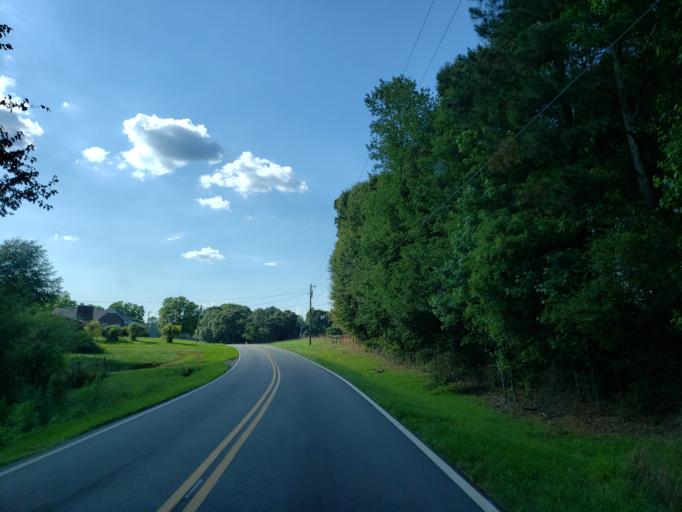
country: US
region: Georgia
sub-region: Haralson County
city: Bremen
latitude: 33.6647
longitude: -85.1132
